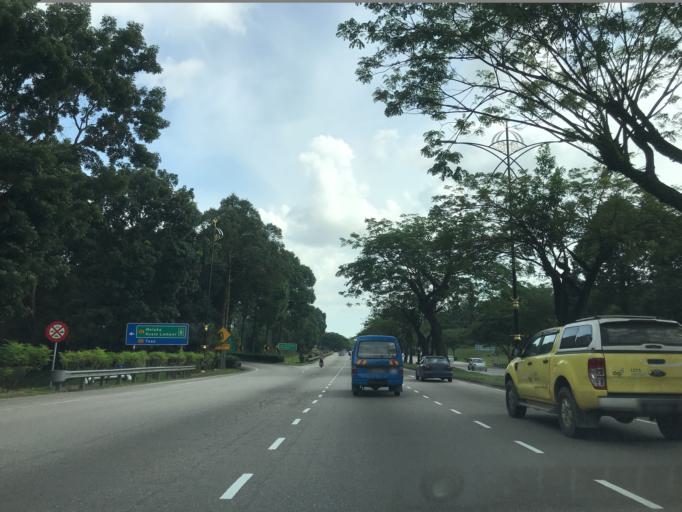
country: MY
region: Johor
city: Taman Senai
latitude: 1.5758
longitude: 103.6586
